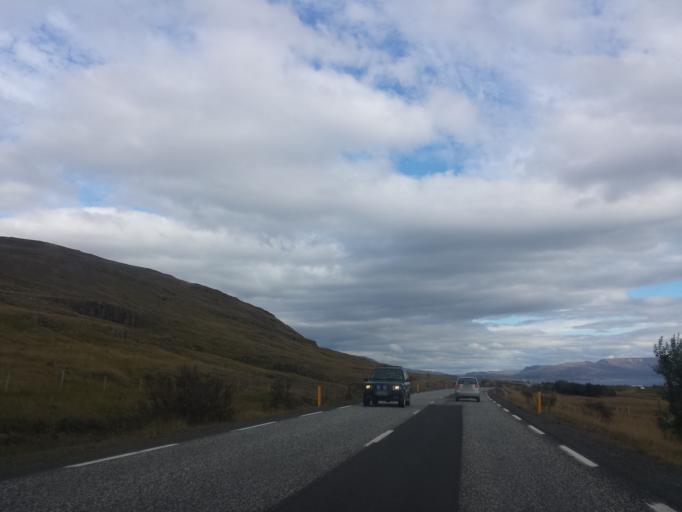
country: IS
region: Capital Region
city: Reykjavik
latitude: 64.3288
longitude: -21.8559
